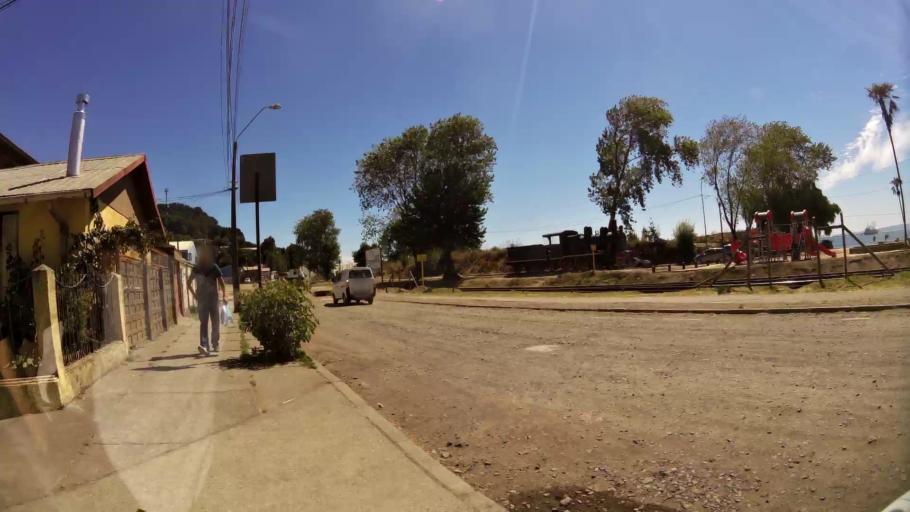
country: CL
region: Biobio
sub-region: Provincia de Concepcion
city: Penco
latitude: -36.7378
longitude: -72.9993
